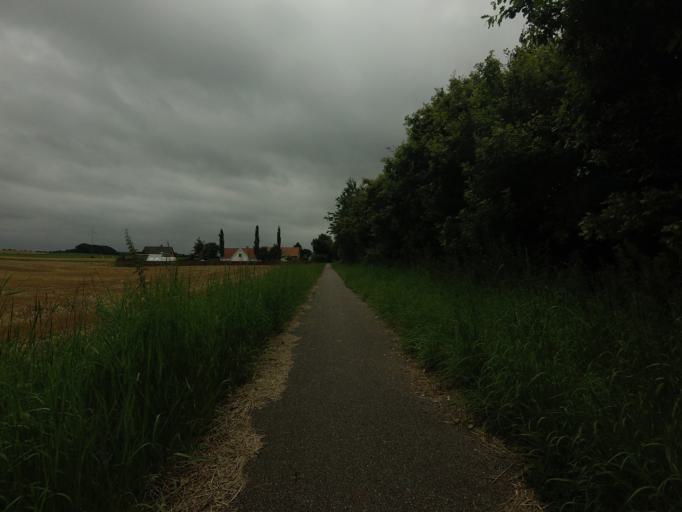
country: DK
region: Central Jutland
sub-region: Horsens Kommune
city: Braedstrup
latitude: 55.9991
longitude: 9.5890
